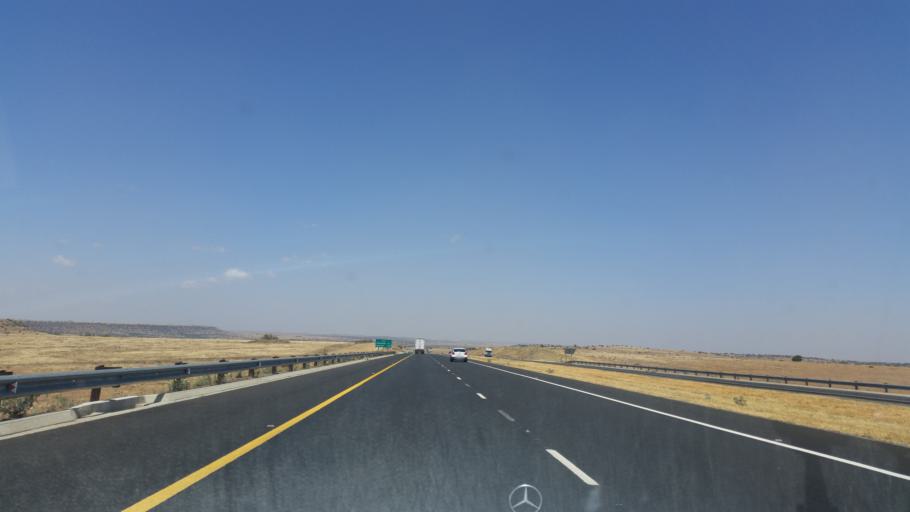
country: ZA
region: Orange Free State
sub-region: Lejweleputswa District Municipality
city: Winburg
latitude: -28.5080
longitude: 26.9941
